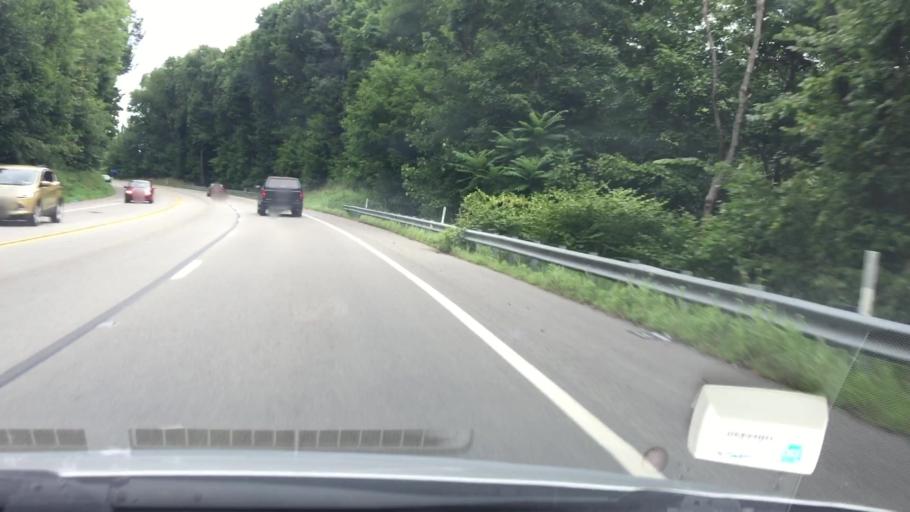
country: US
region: Pennsylvania
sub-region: Westmoreland County
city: Arnold
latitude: 40.5825
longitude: -79.7477
